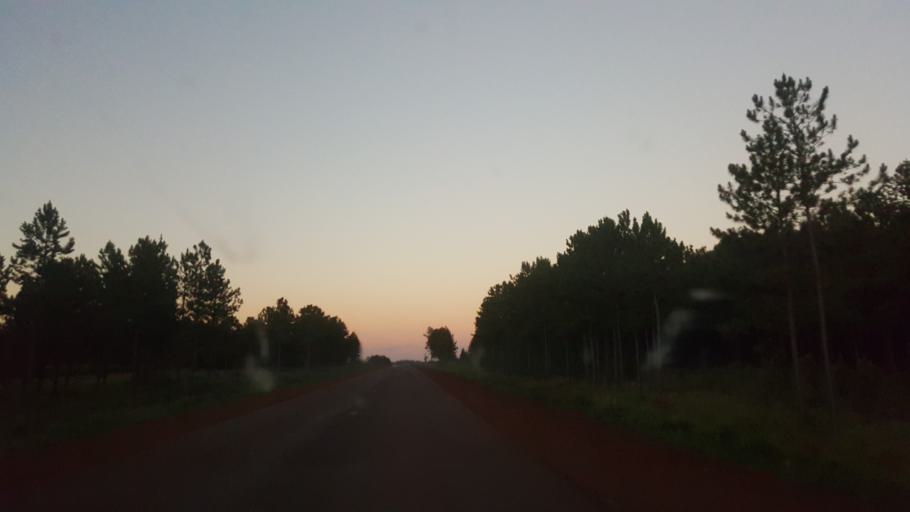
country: AR
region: Corrientes
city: Garruchos
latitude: -28.2232
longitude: -55.7986
